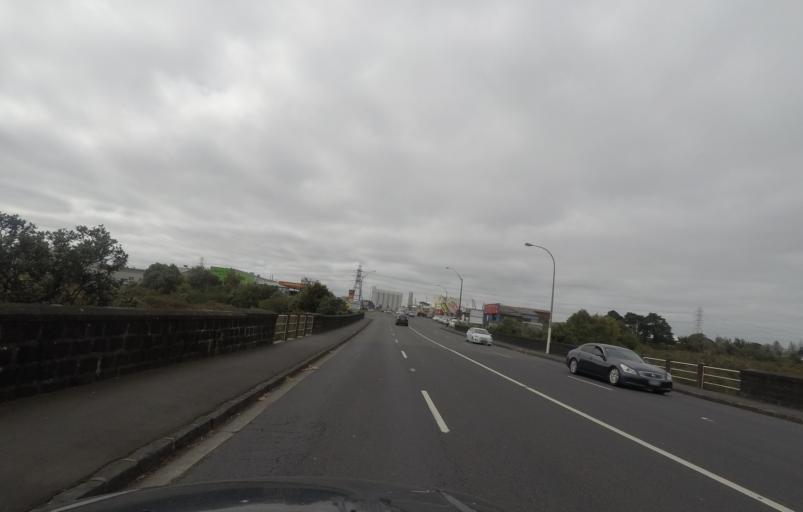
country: NZ
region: Auckland
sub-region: Auckland
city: Wiri
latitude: -36.9550
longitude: 174.8495
